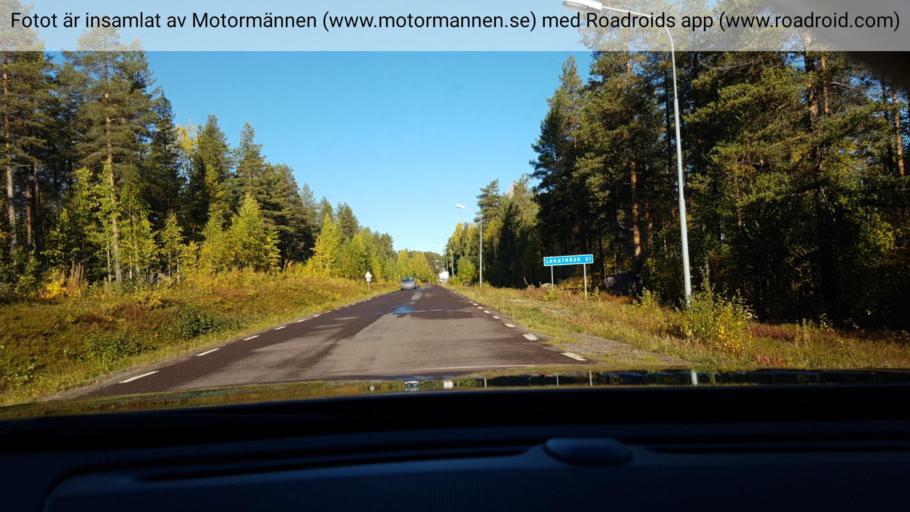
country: SE
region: Norrbotten
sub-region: Bodens Kommun
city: Boden
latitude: 66.1195
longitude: 21.3318
